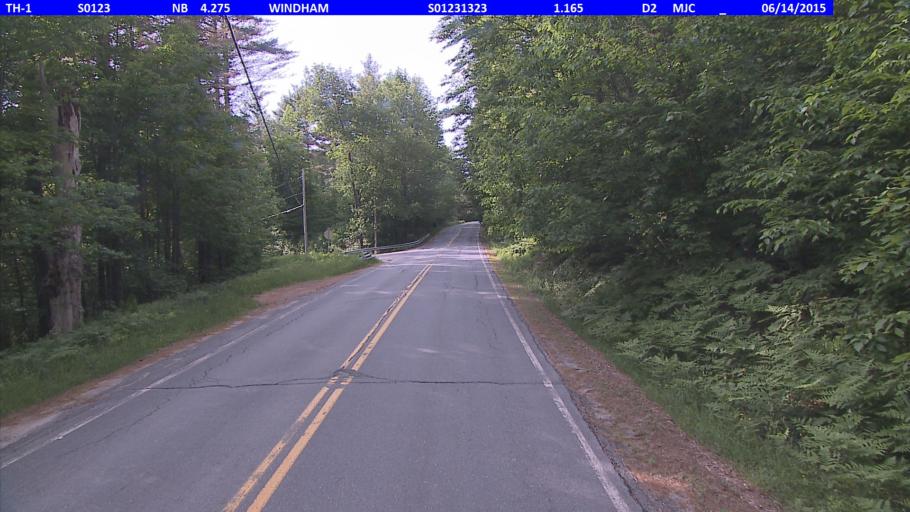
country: US
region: Vermont
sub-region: Windham County
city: Newfane
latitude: 43.1424
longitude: -72.7188
